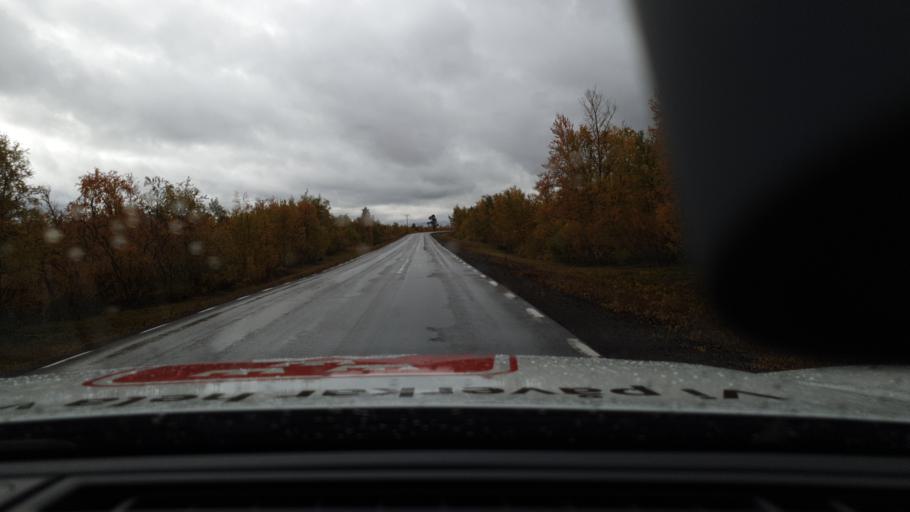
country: SE
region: Norrbotten
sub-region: Kiruna Kommun
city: Kiruna
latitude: 67.7833
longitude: 20.2269
